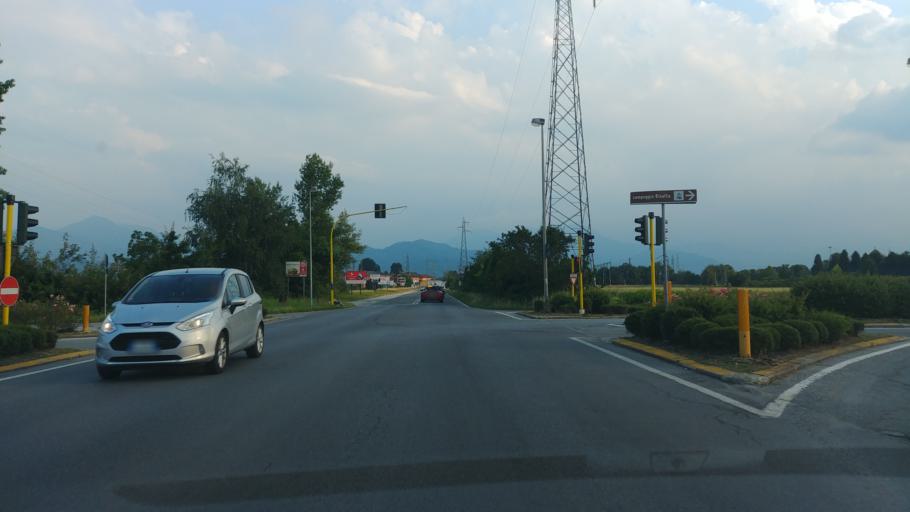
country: IT
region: Piedmont
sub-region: Provincia di Cuneo
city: San Defendente
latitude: 44.3660
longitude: 7.5184
